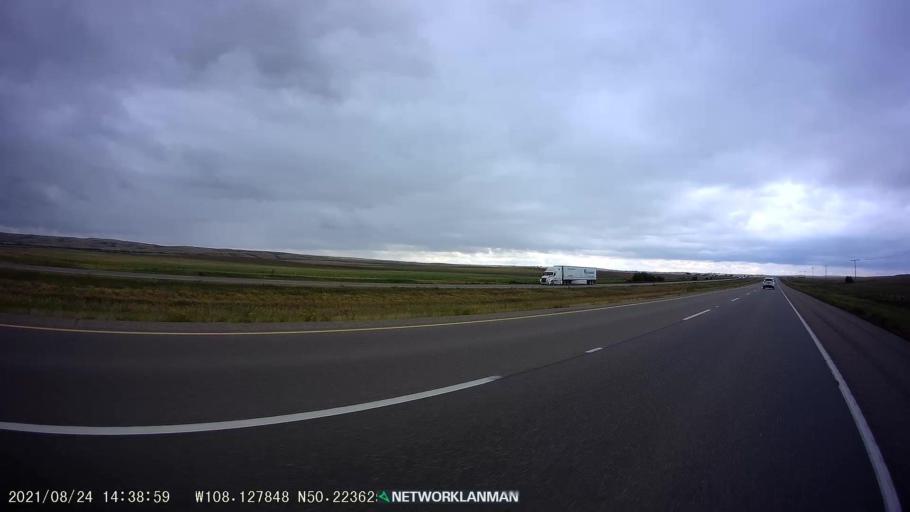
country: CA
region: Saskatchewan
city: Swift Current
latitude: 50.2237
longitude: -108.1287
